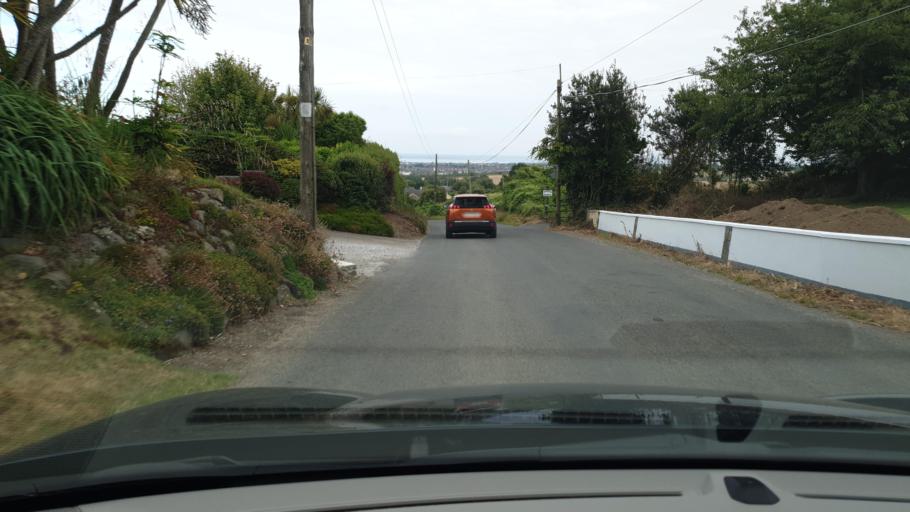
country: IE
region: Leinster
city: Balrothery
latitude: 53.5806
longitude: -6.1512
